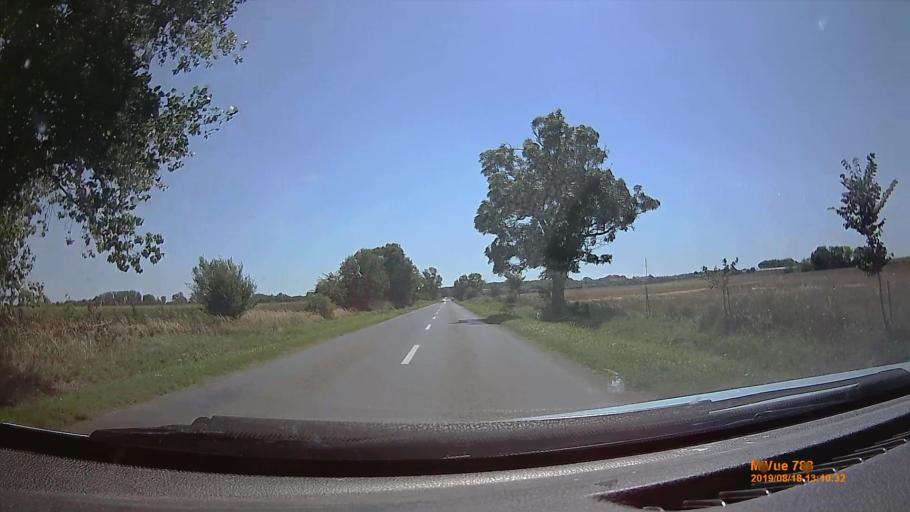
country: HU
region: Fejer
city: Kaloz
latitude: 46.9135
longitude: 18.5168
